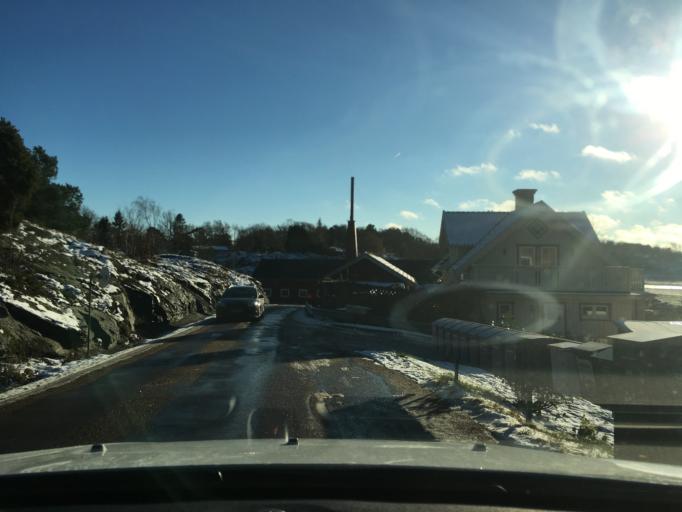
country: SE
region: Vaestra Goetaland
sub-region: Tjorns Kommun
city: Myggenas
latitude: 58.0895
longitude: 11.7504
